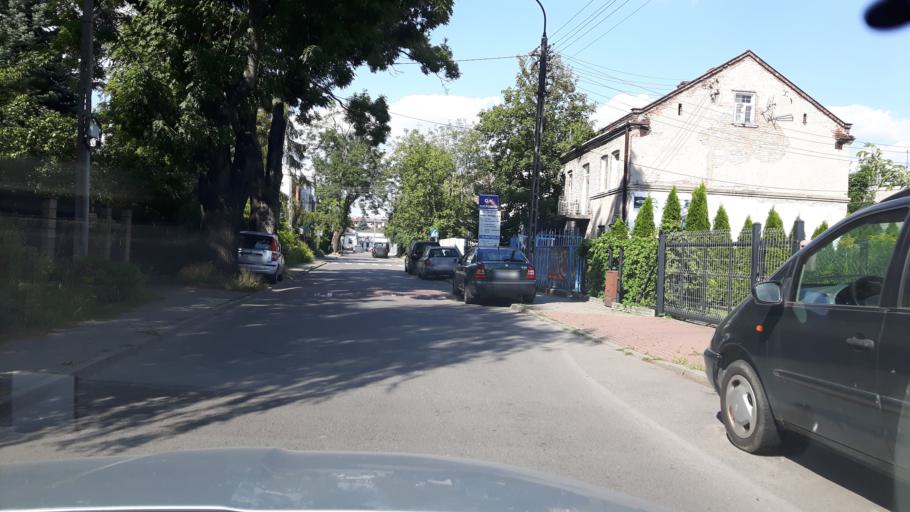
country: PL
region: Masovian Voivodeship
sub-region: Warszawa
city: Wlochy
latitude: 52.2030
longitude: 20.9211
